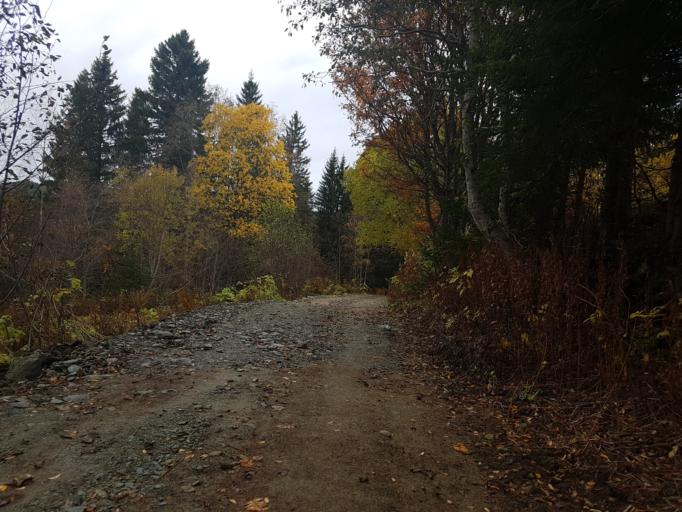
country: NO
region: Sor-Trondelag
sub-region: Trondheim
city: Trondheim
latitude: 63.3995
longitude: 10.2936
